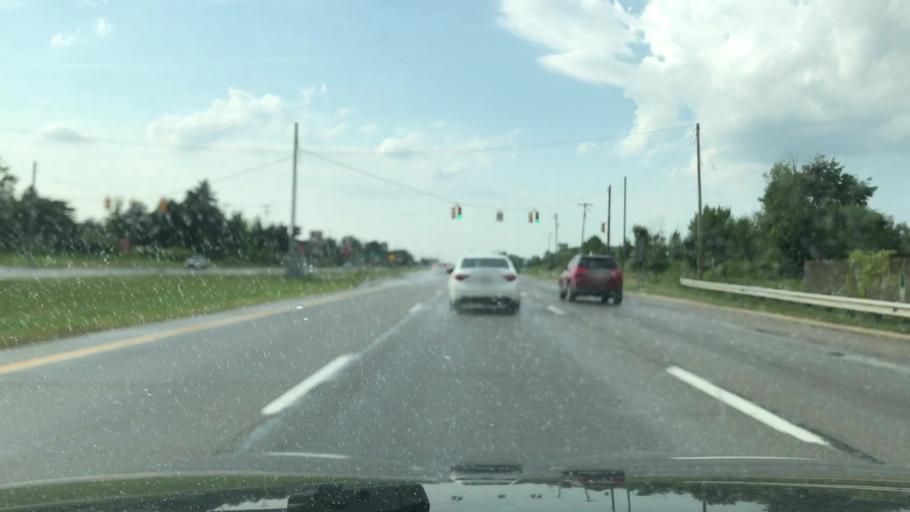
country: US
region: Michigan
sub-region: Kent County
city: Caledonia
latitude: 42.8574
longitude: -85.5441
